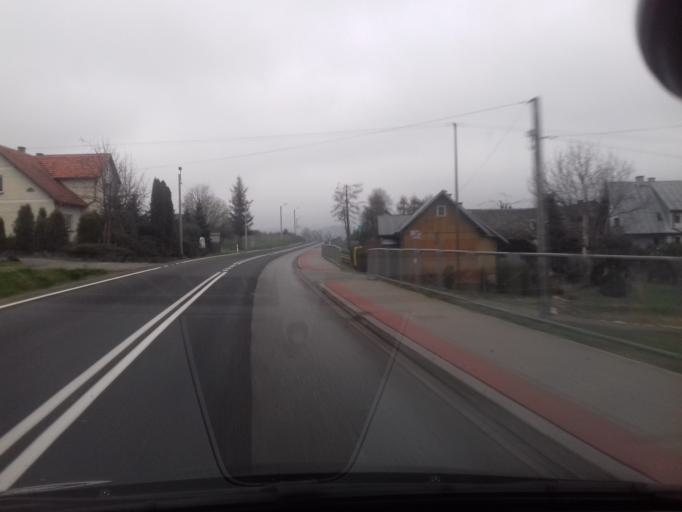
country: PL
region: Lesser Poland Voivodeship
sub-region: Powiat limanowski
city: Dobra
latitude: 49.7207
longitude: 20.2686
